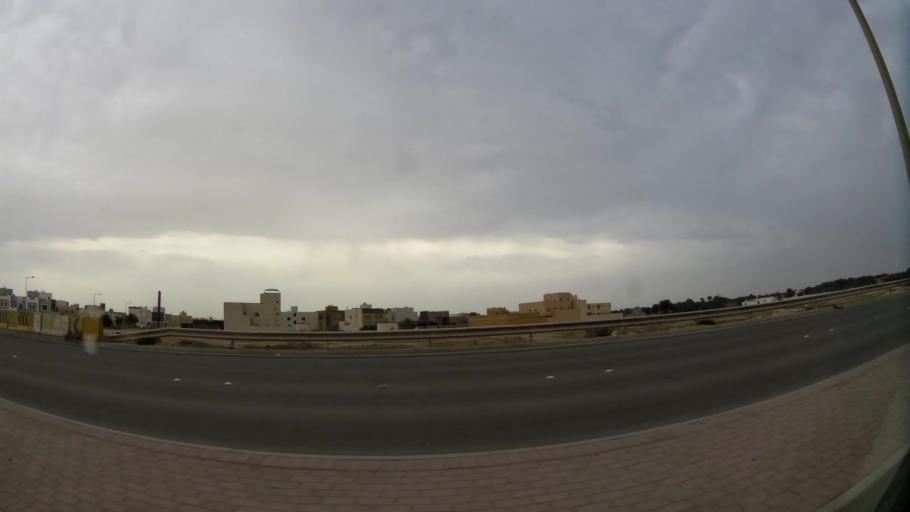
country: BH
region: Central Governorate
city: Madinat Hamad
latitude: 26.1119
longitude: 50.4878
